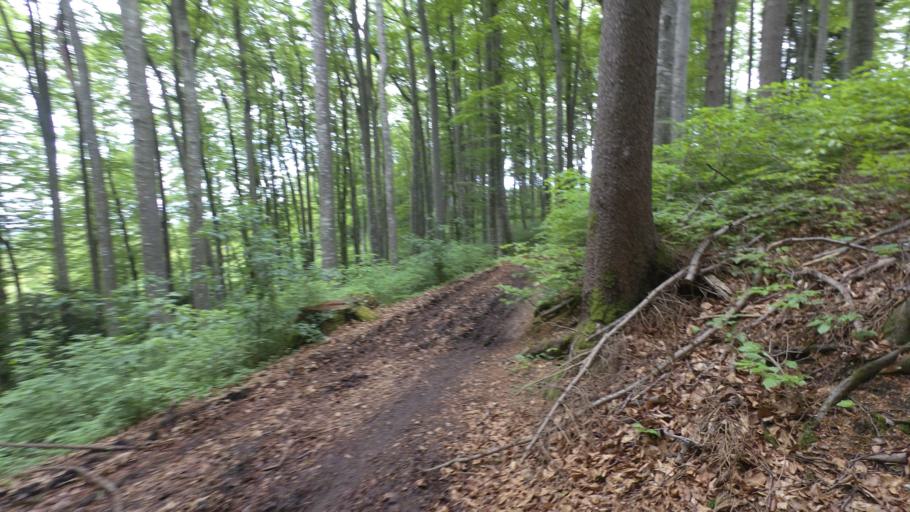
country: DE
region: Bavaria
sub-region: Upper Bavaria
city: Vachendorf
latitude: 47.8333
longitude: 12.6097
